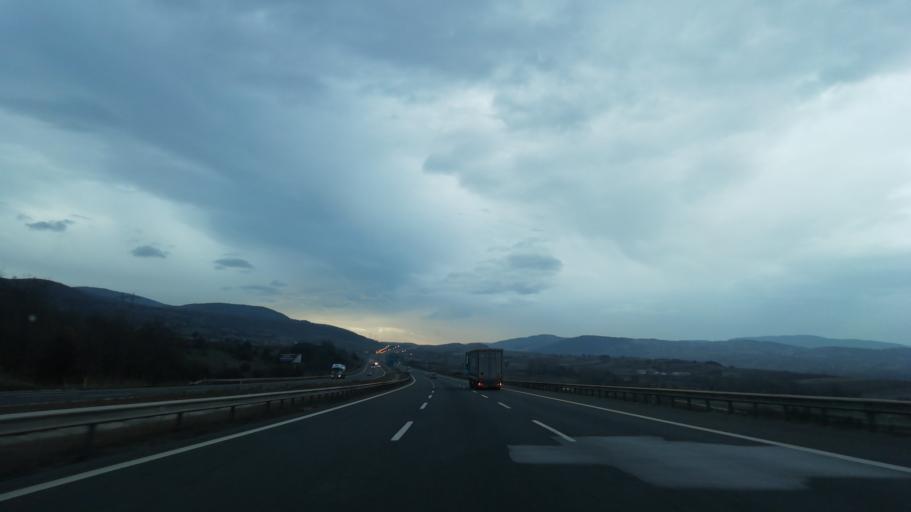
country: TR
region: Bolu
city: Yenicaga
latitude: 40.7657
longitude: 32.0245
